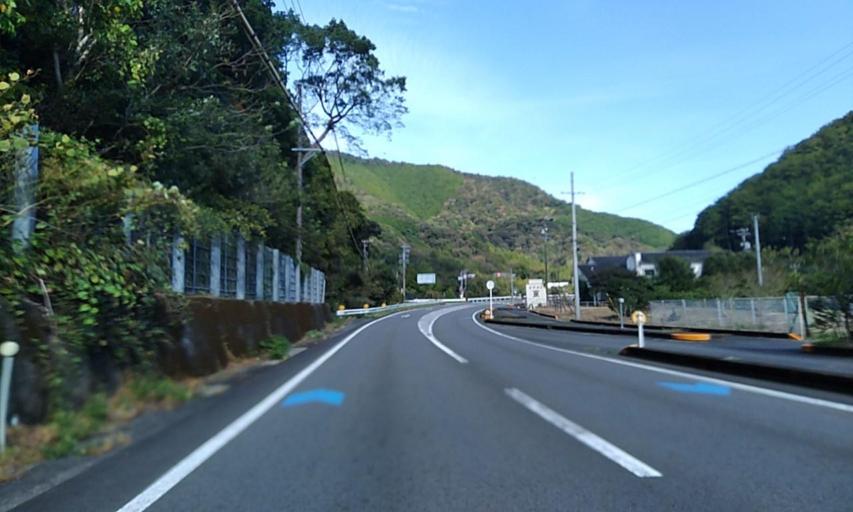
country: JP
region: Mie
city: Owase
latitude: 34.1947
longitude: 136.3152
